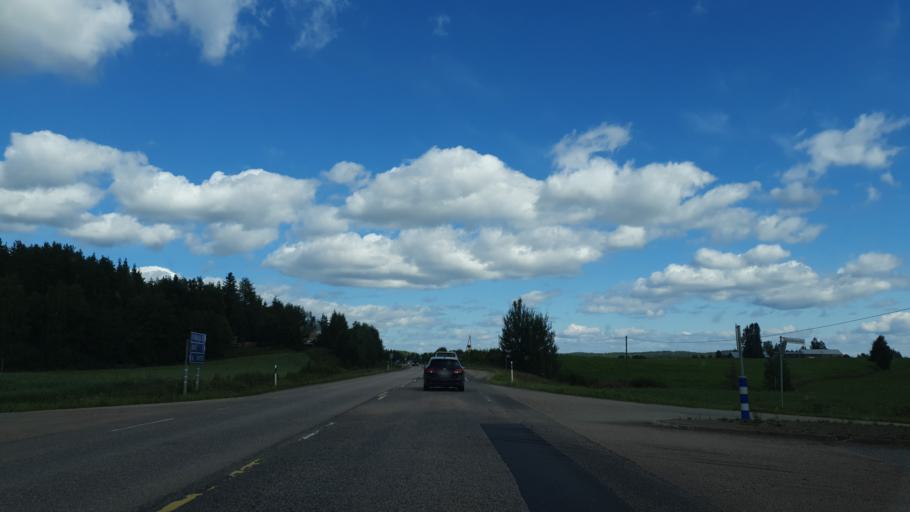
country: FI
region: Central Finland
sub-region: Jaemsae
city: Jaemsae
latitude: 61.8365
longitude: 25.1139
